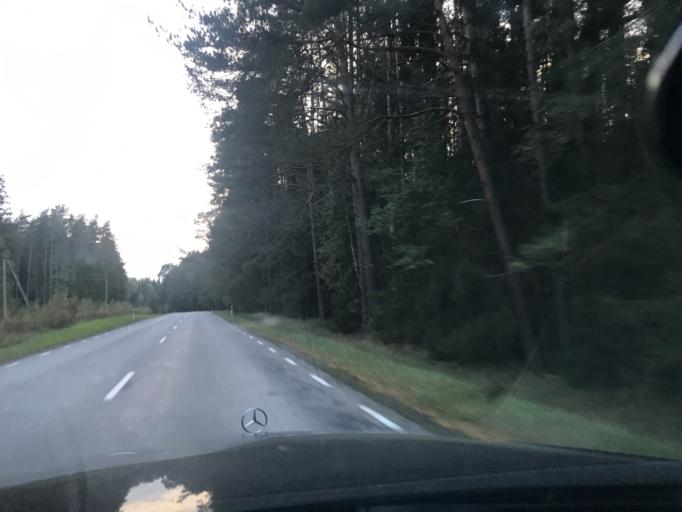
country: EE
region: Valgamaa
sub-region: Torva linn
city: Torva
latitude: 58.0101
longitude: 26.1082
